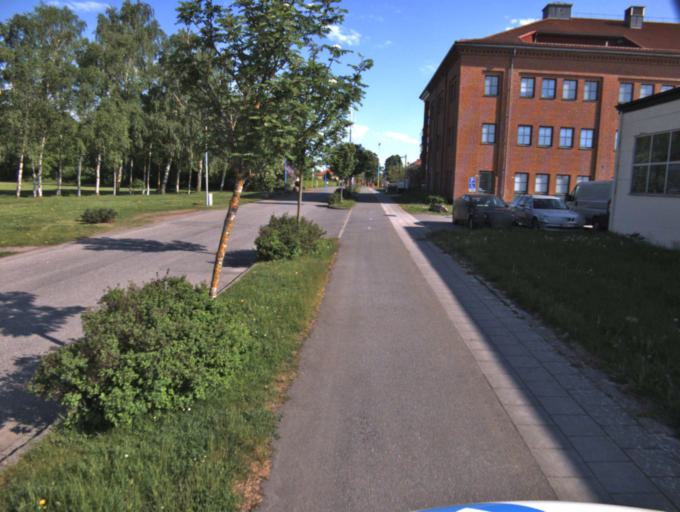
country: SE
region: Skane
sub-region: Kristianstads Kommun
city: Kristianstad
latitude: 56.0448
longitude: 14.1467
